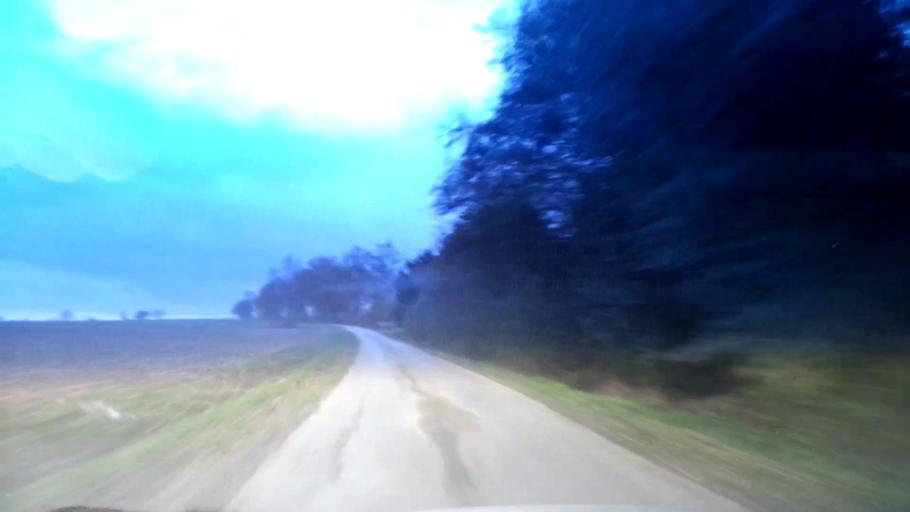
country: DE
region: Bavaria
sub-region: Upper Palatinate
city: Fuchsmuhl
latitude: 49.9247
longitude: 12.1620
